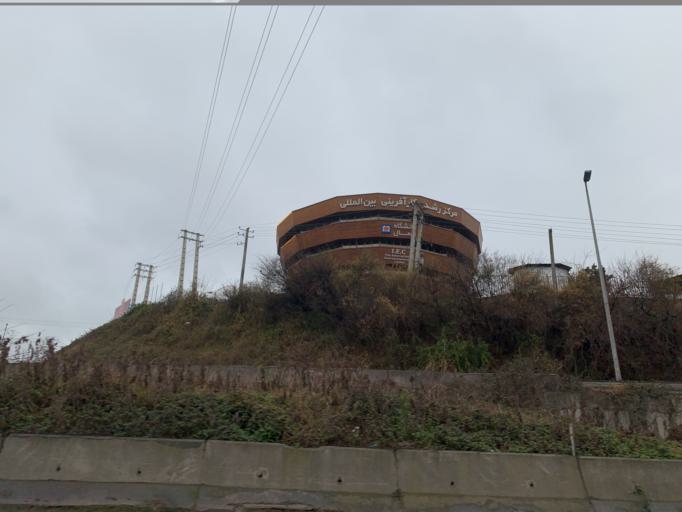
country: IR
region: Mazandaran
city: Amol
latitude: 36.4002
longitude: 52.3465
